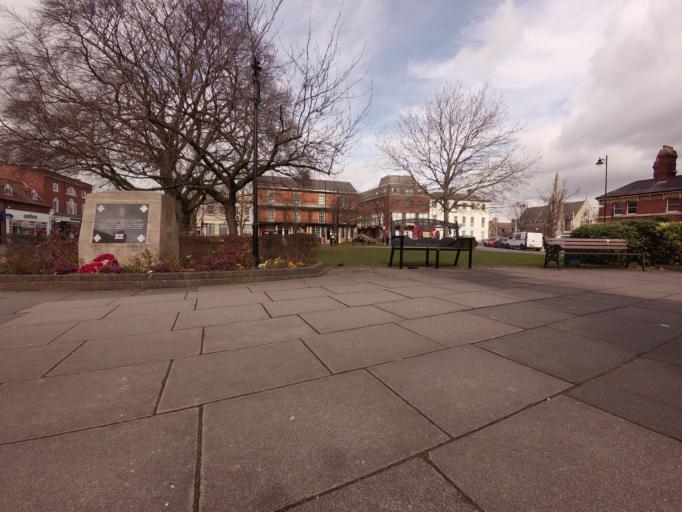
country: GB
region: England
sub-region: Lincolnshire
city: Grantham
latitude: 52.9105
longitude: -0.6409
